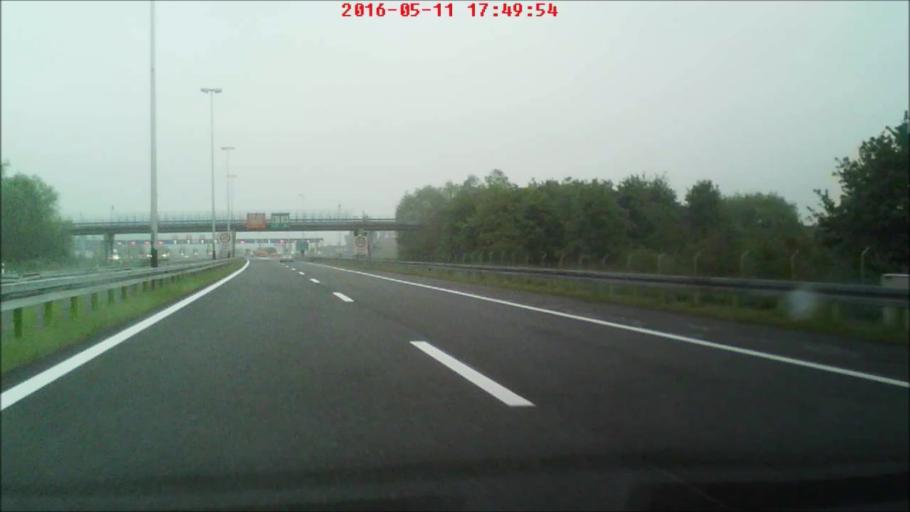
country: HR
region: Zagrebacka
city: Jablanovec
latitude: 45.8801
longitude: 15.8283
